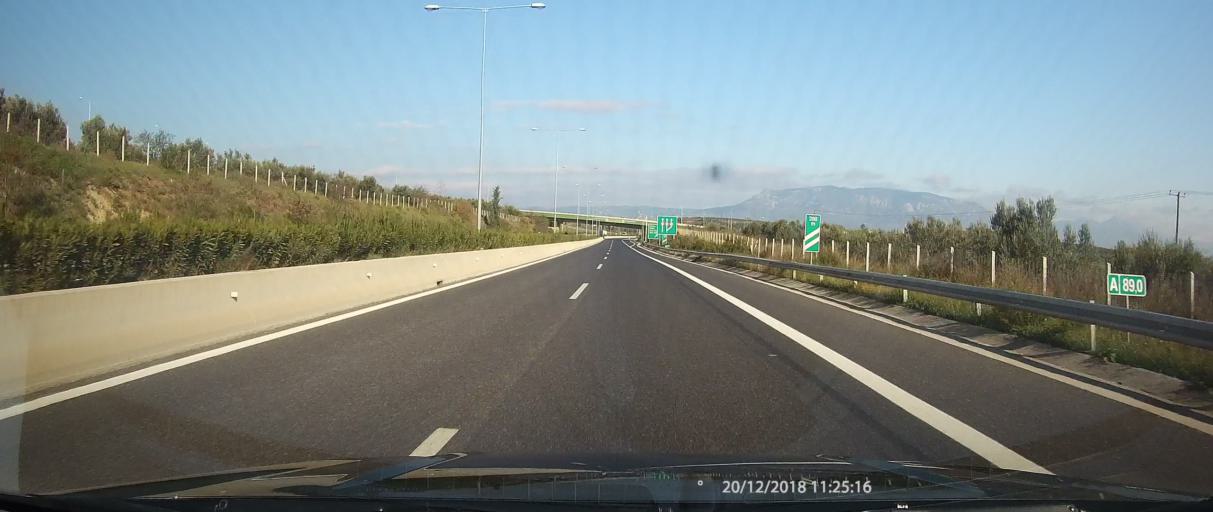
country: GR
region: Peloponnese
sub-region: Nomos Korinthias
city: Arkhaia Korinthos
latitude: 37.8938
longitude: 22.8970
